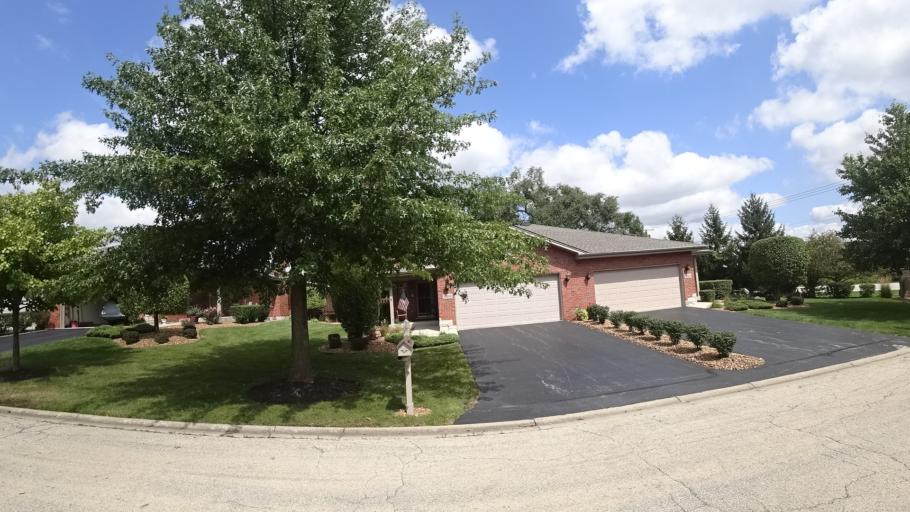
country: US
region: Illinois
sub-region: Cook County
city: Orland Hills
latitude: 41.5723
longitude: -87.8718
